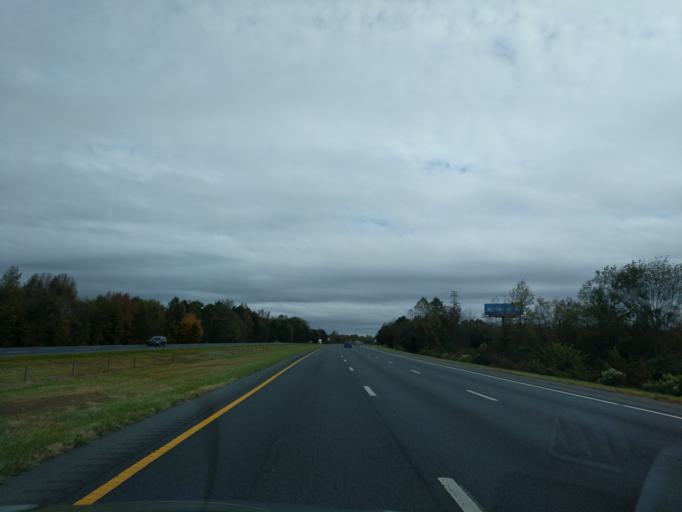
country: US
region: North Carolina
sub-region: Davidson County
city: Lexington
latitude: 35.7758
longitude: -80.3060
